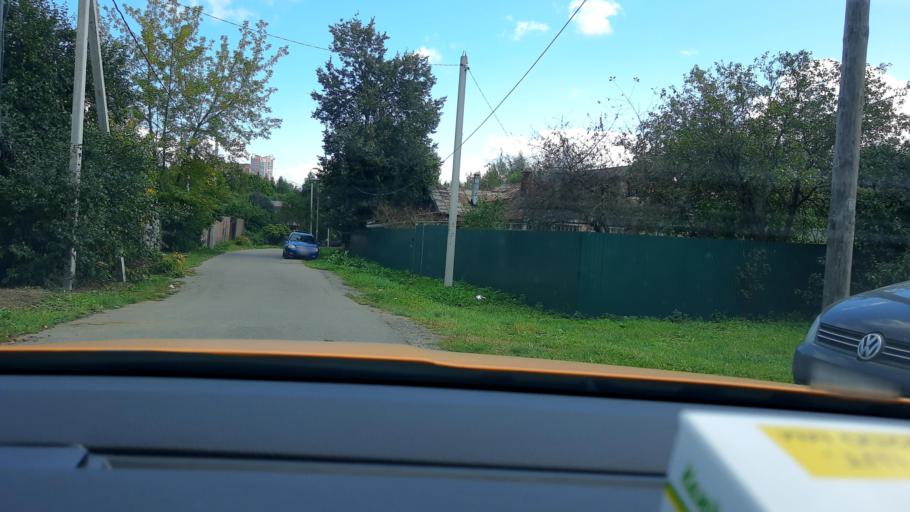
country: RU
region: Moscow
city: Annino
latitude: 55.5482
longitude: 37.5713
